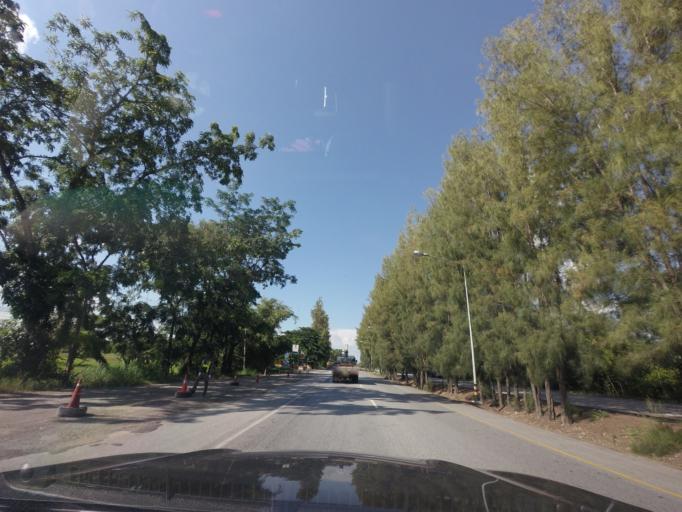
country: TH
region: Nakhon Ratchasima
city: Sida
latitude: 15.5373
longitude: 102.5455
